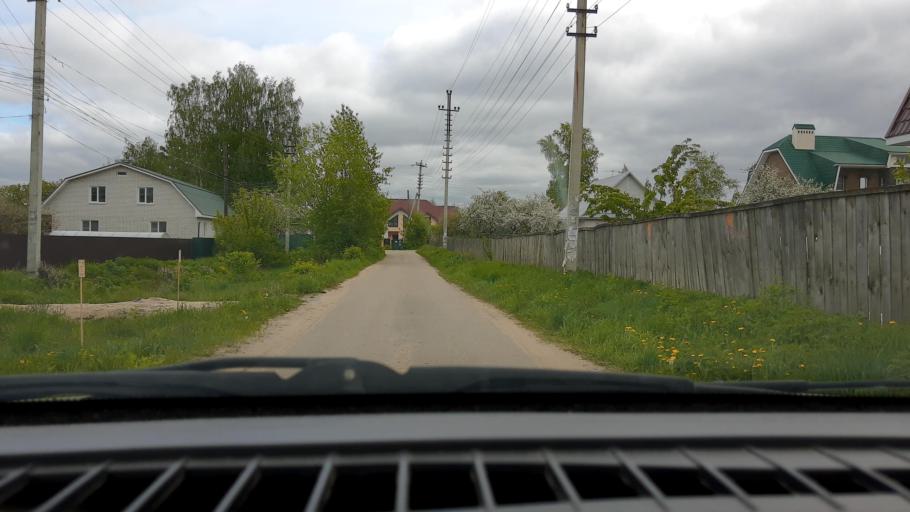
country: RU
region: Nizjnij Novgorod
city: Lukino
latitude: 56.4083
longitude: 43.7096
